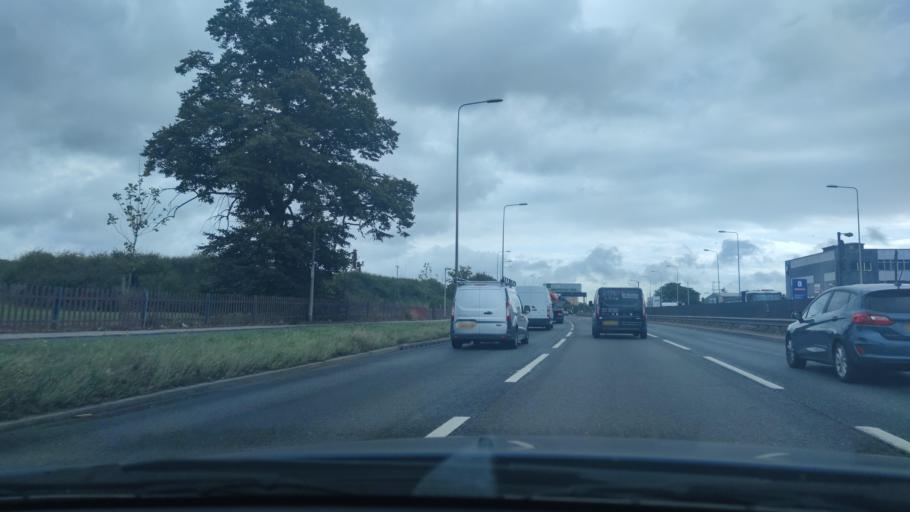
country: GB
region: England
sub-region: Greater London
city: Becontree
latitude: 51.5316
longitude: 0.1249
